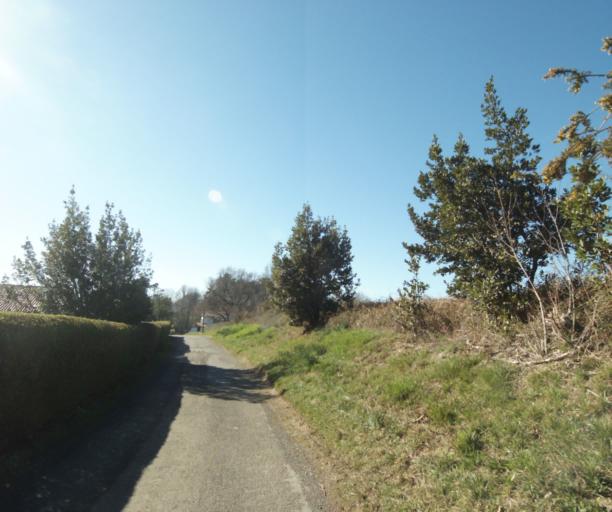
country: FR
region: Aquitaine
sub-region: Departement des Pyrenees-Atlantiques
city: Urrugne
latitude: 43.3696
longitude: -1.7304
